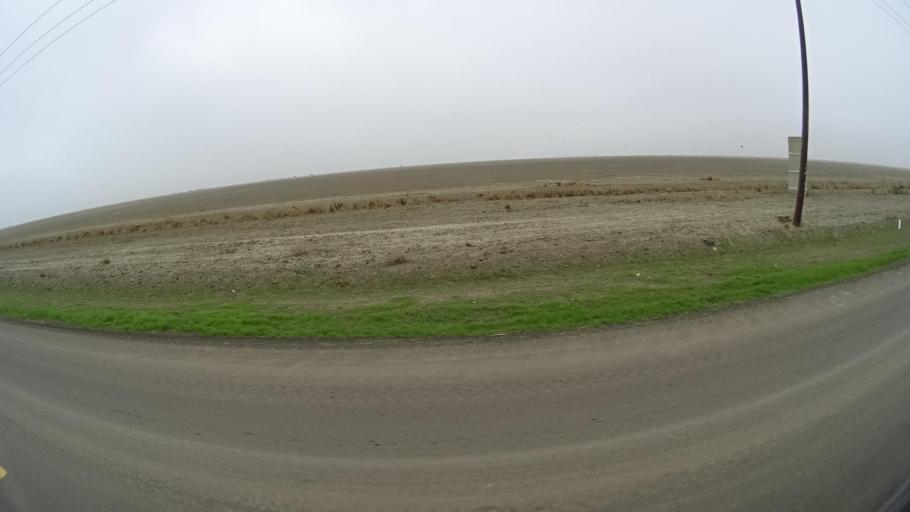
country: US
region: California
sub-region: Tulare County
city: Alpaugh
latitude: 35.7028
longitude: -119.5025
